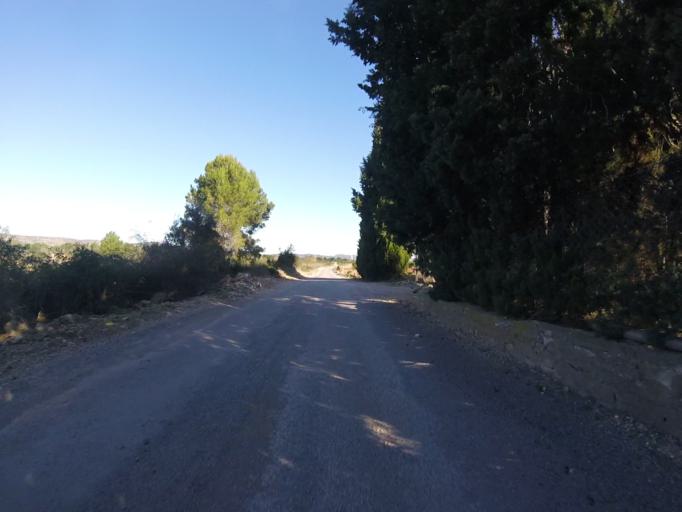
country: ES
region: Valencia
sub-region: Provincia de Castello
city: Alcala de Xivert
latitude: 40.2872
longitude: 0.2140
